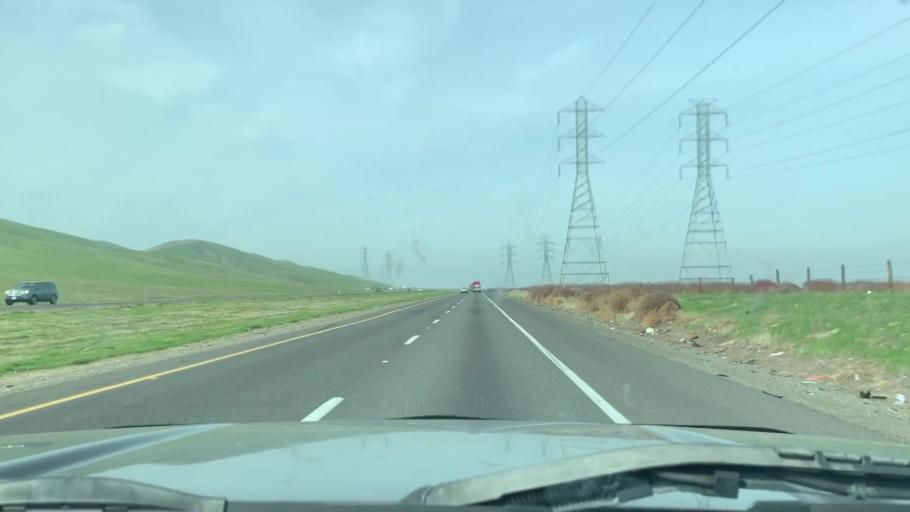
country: US
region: California
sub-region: Merced County
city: South Dos Palos
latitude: 36.8848
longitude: -120.7975
